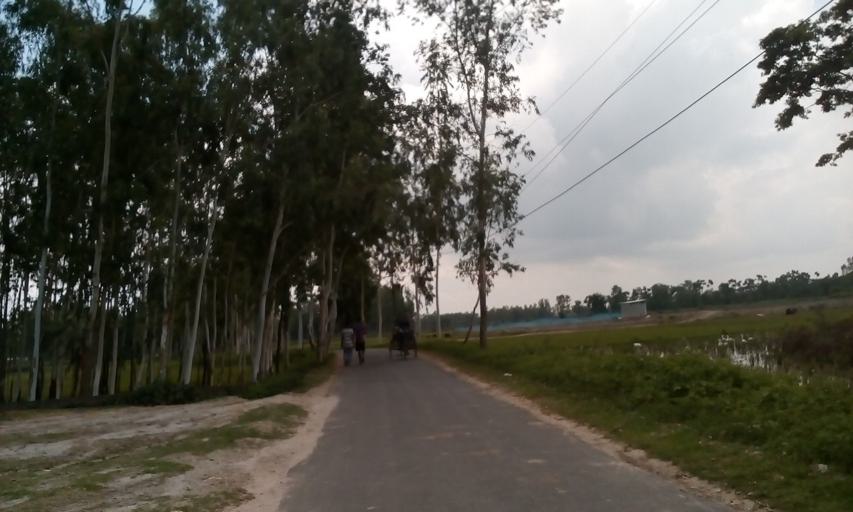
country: IN
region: West Bengal
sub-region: Dakshin Dinajpur
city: Balurghat
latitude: 25.3780
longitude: 88.9957
